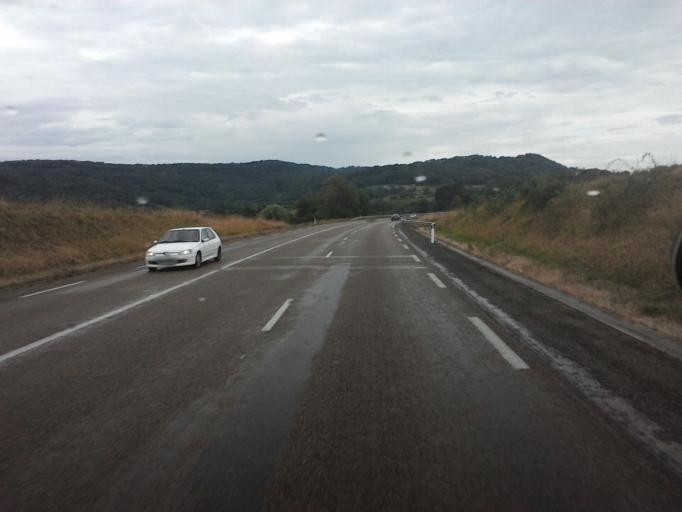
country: FR
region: Franche-Comte
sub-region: Departement du Jura
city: Arbois
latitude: 46.9065
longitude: 5.7654
